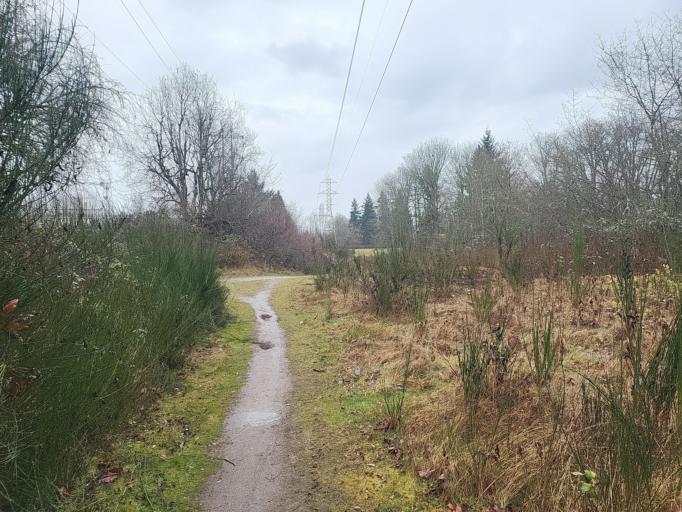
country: US
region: Washington
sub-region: King County
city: Renton
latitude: 47.4669
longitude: -122.1948
